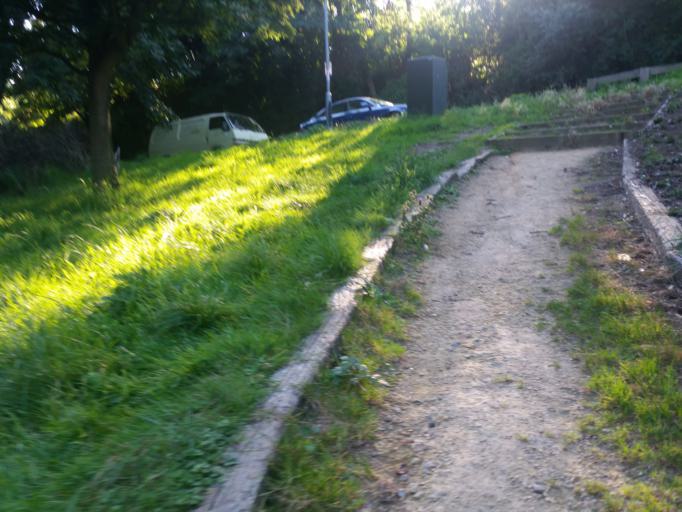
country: GB
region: England
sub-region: East Sussex
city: Hastings
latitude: 50.8611
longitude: 0.5940
